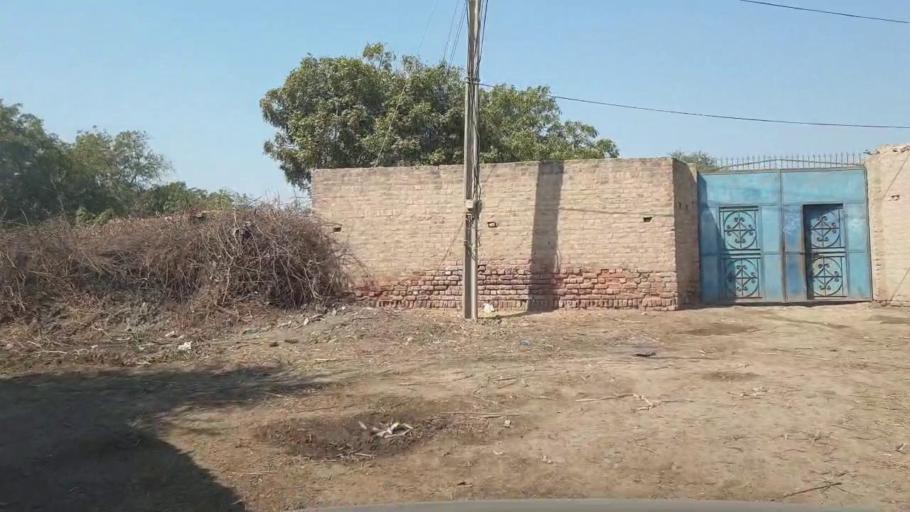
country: PK
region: Sindh
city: Tando Jam
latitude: 25.3295
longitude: 68.6280
